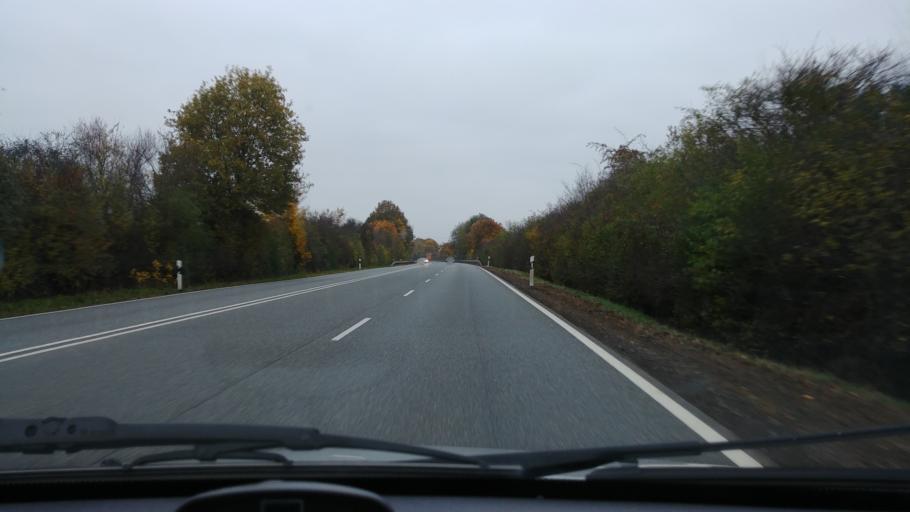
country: DE
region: Hesse
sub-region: Regierungsbezirk Giessen
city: Dehrn
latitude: 50.4511
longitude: 8.0872
